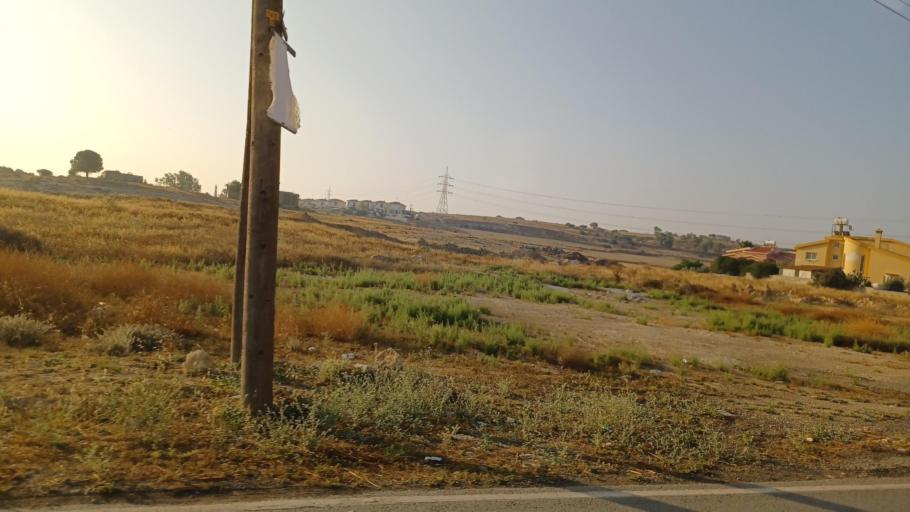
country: CY
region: Larnaka
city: Pyla
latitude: 35.0055
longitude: 33.6918
